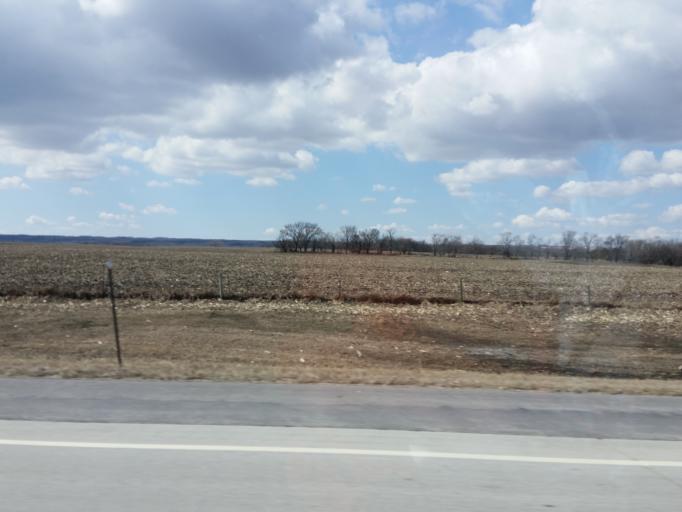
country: US
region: South Dakota
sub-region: Roberts County
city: Sisseton
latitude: 45.4885
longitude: -96.9896
